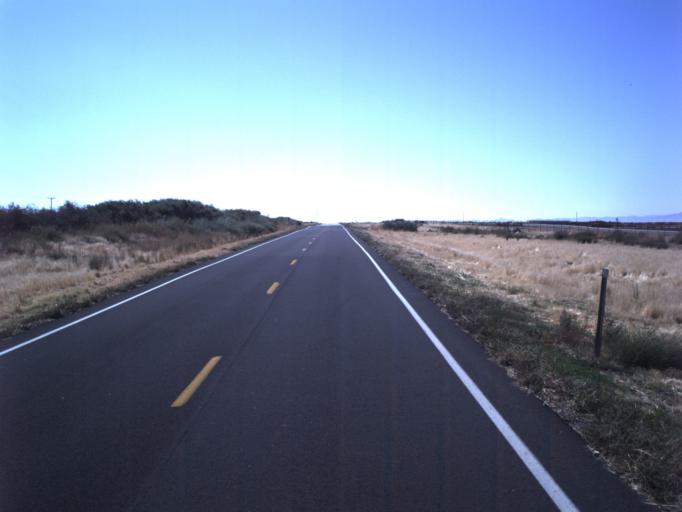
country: US
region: Utah
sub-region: Tooele County
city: Grantsville
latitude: 40.5307
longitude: -112.7477
